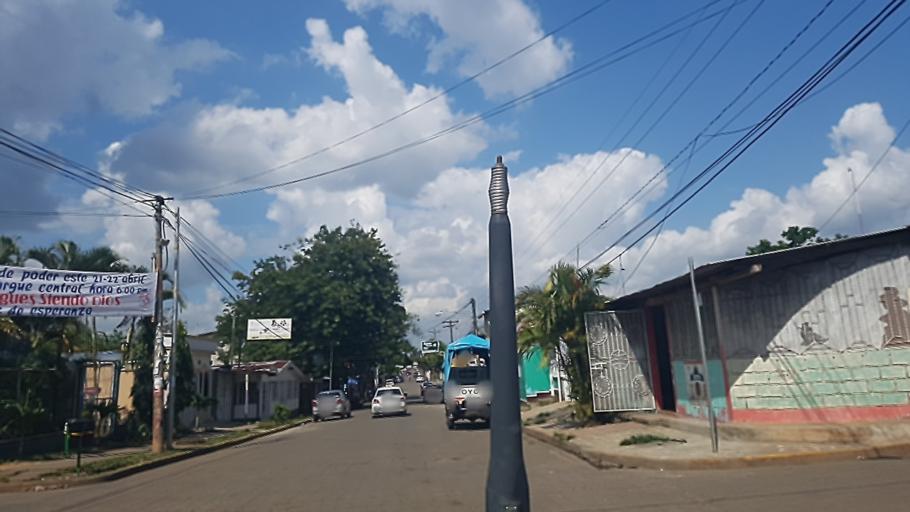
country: NI
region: Atlantico Sur
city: Nueva Guinea
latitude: 11.6882
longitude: -84.4575
